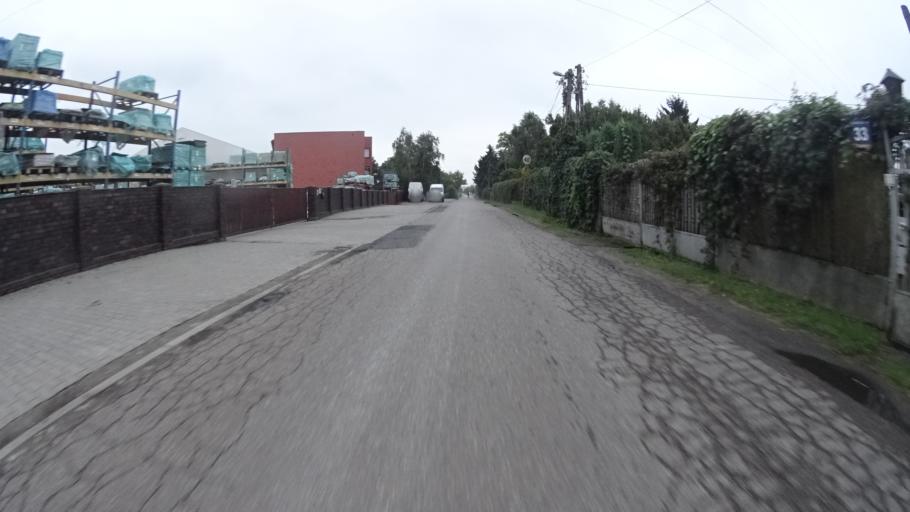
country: PL
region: Masovian Voivodeship
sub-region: Warszawa
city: Ursus
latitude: 52.2204
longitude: 20.8805
